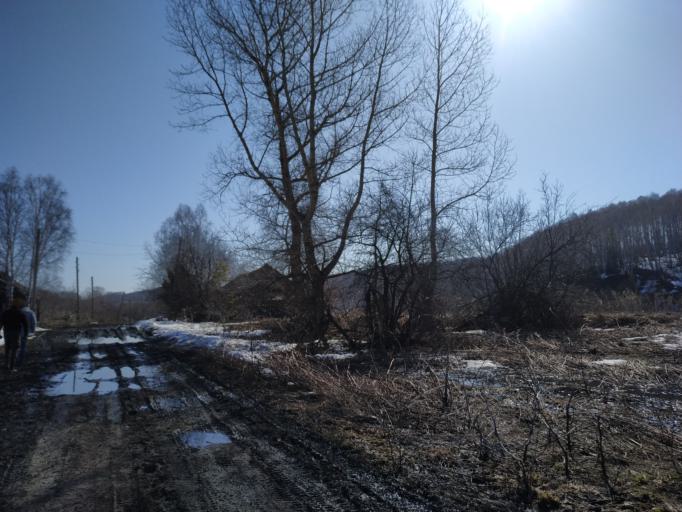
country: RU
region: Altai Krai
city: Krasnogorskoye
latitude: 52.4820
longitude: 86.2220
